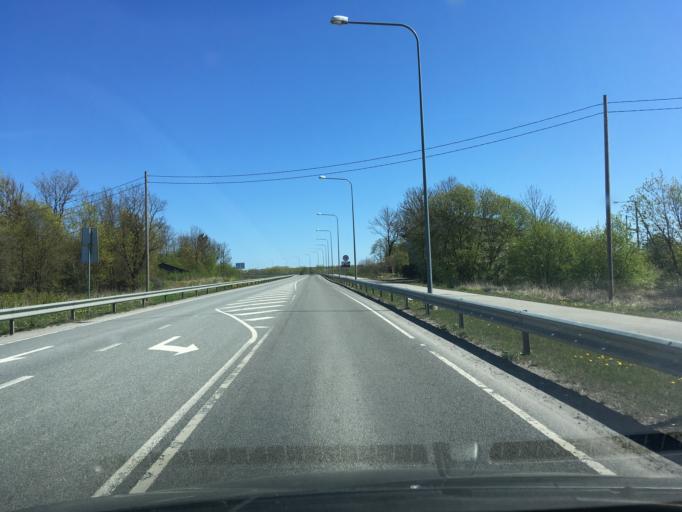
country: EE
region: Harju
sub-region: Joelaehtme vald
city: Loo
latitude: 59.4530
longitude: 24.9694
